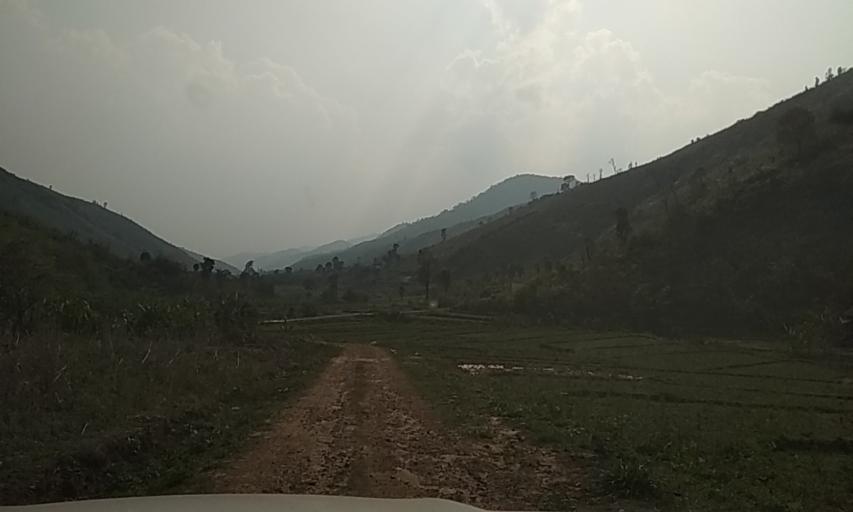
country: LA
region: Louangphabang
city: Louangphabang
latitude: 20.0357
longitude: 101.7950
